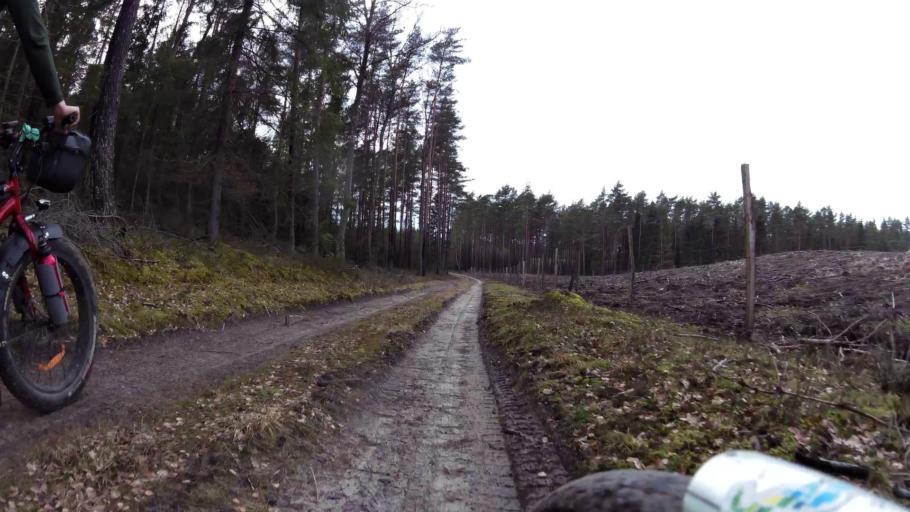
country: PL
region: Pomeranian Voivodeship
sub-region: Powiat bytowski
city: Trzebielino
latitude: 54.1510
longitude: 17.1735
